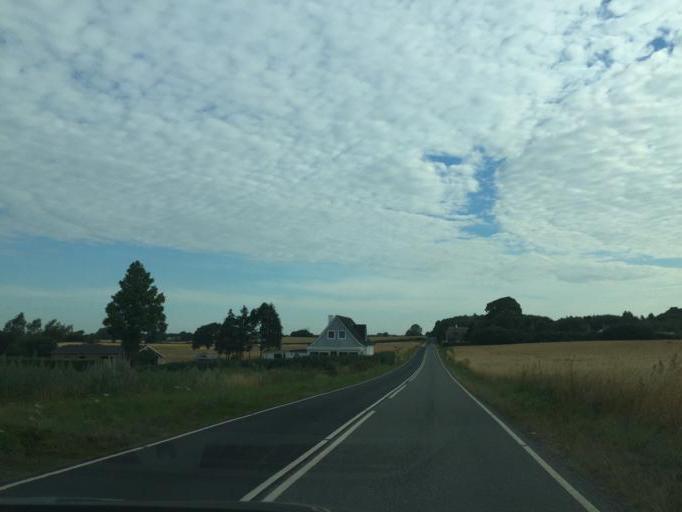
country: DK
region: South Denmark
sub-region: Assens Kommune
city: Assens
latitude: 55.2909
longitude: 9.9810
